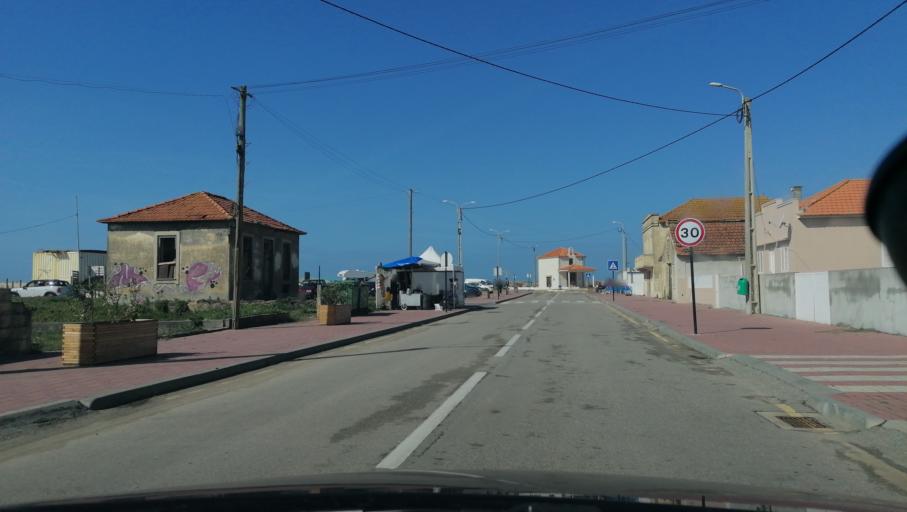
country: PT
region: Aveiro
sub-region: Espinho
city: Silvalde
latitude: 40.9779
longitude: -8.6480
